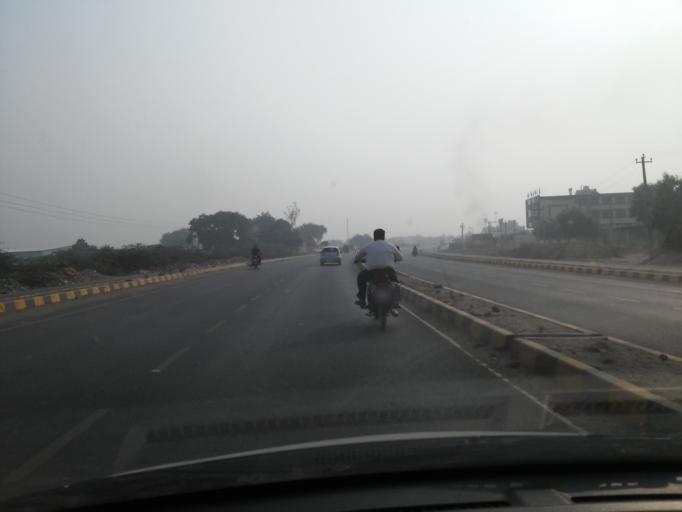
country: IN
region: Gujarat
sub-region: Kachchh
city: Bhuj
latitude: 23.2400
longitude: 69.7162
